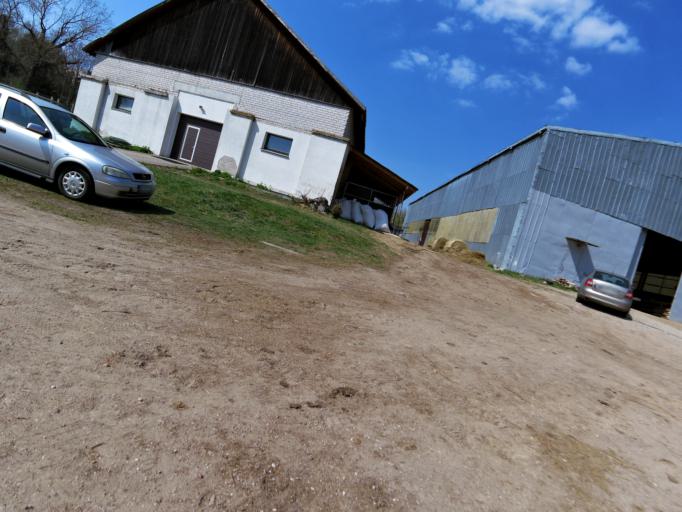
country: LT
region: Vilnius County
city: Justiniskes
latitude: 54.7183
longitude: 25.1992
